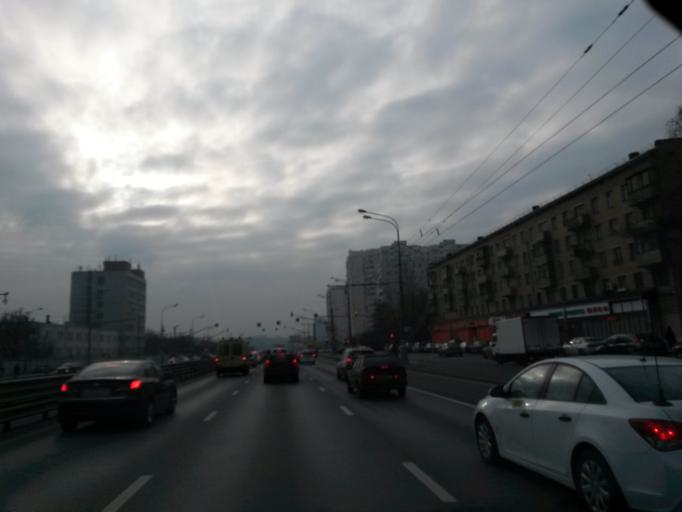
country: RU
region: Moscow
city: Nagornyy
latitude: 55.6467
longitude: 37.6195
